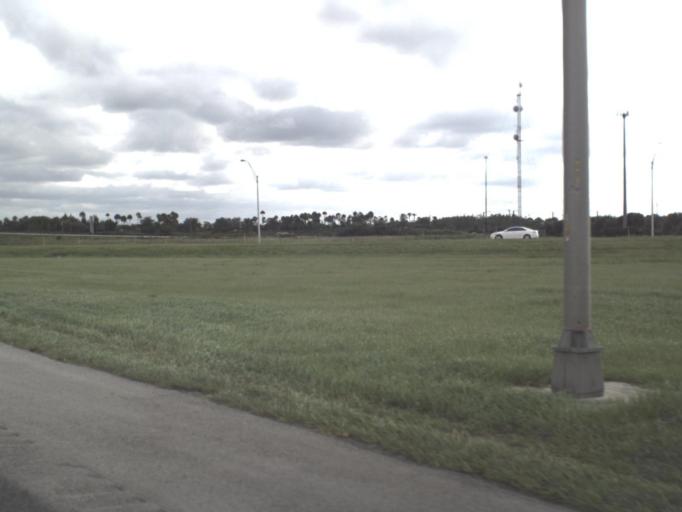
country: US
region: Florida
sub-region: Palm Beach County
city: Limestone Creek
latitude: 26.9391
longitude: -80.1558
